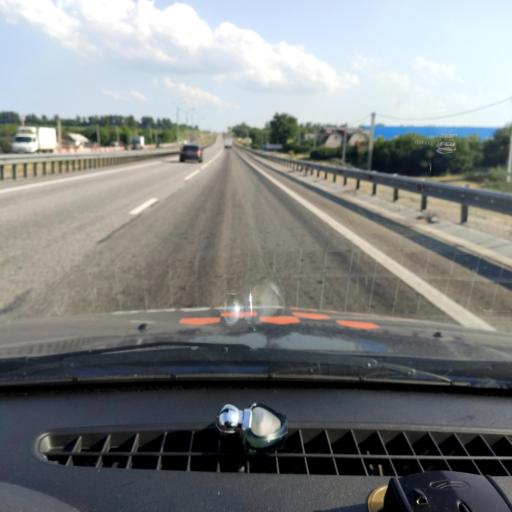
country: RU
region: Voronezj
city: Ramon'
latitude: 52.0379
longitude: 39.1984
